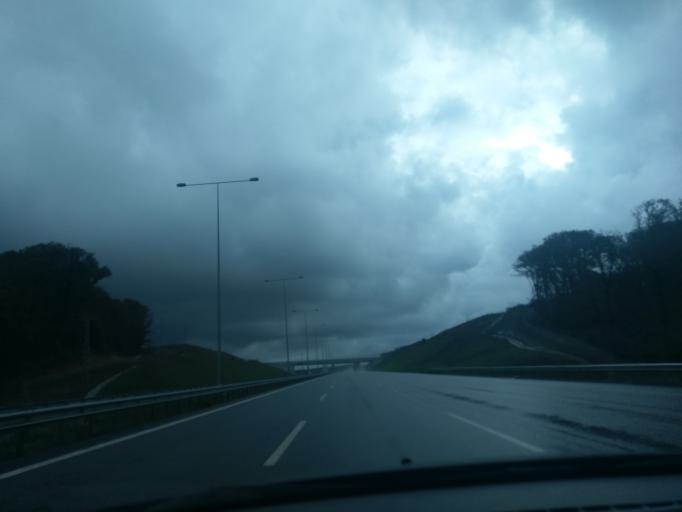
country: TR
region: Istanbul
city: Kemerburgaz
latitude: 41.2353
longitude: 28.8968
